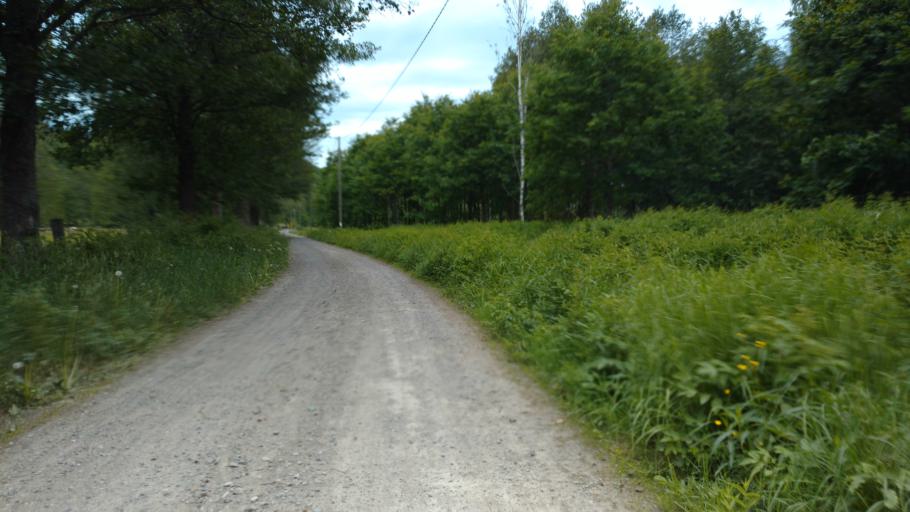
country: FI
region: Uusimaa
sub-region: Raaseporin
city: Pohja
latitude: 60.1219
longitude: 23.5389
